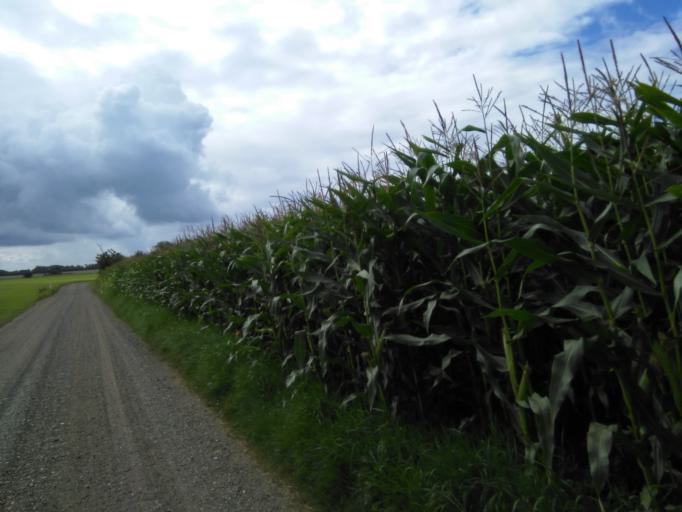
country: DK
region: Central Jutland
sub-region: Odder Kommune
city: Odder
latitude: 55.8718
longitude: 10.1471
